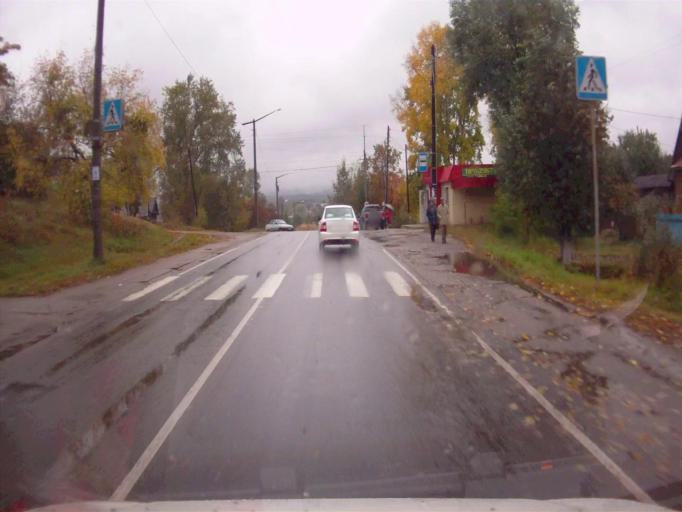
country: RU
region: Chelyabinsk
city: Kyshtym
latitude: 55.7225
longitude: 60.5301
